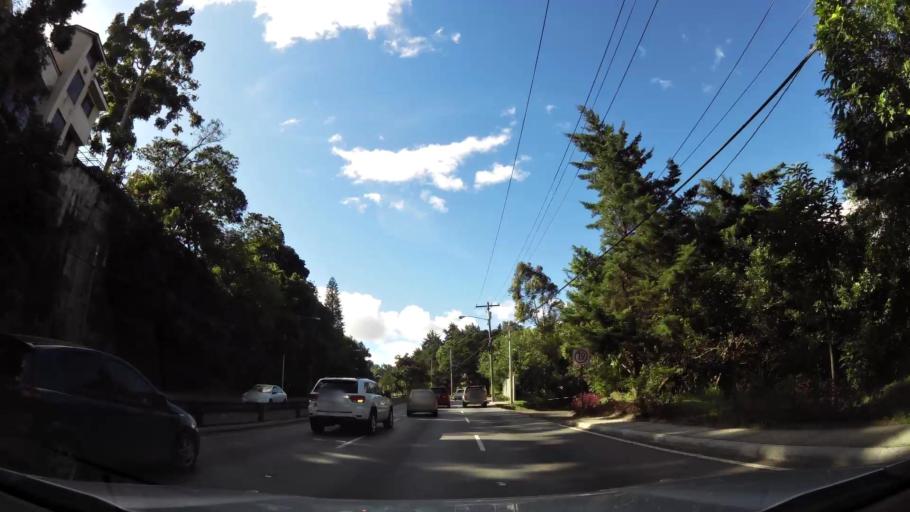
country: GT
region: Guatemala
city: Guatemala City
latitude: 14.6113
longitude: -90.5054
